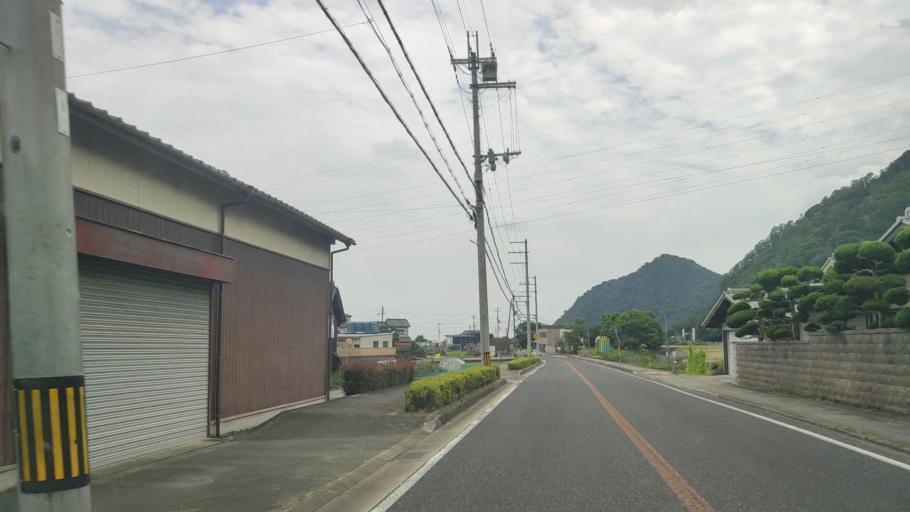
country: JP
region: Hyogo
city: Tatsunocho-tominaga
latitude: 34.8867
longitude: 134.5467
